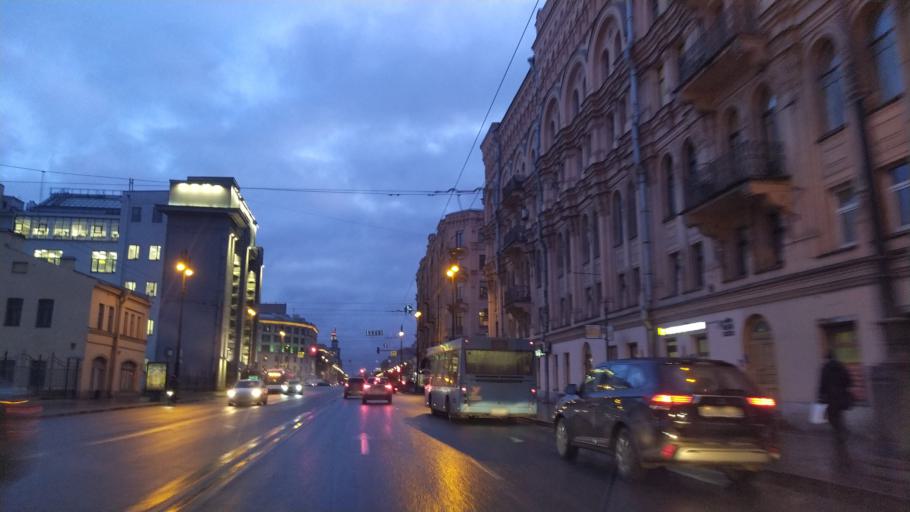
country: RU
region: St.-Petersburg
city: Saint Petersburg
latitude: 59.9103
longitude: 30.3183
